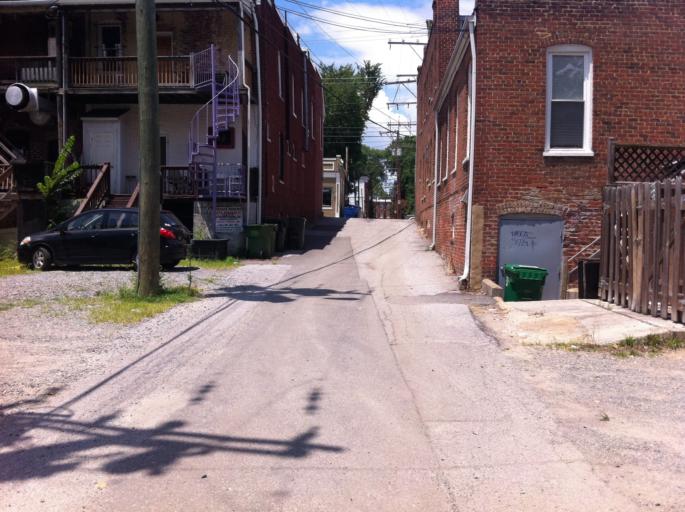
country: US
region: Virginia
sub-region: City of Richmond
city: Richmond
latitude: 37.5555
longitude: -77.4705
